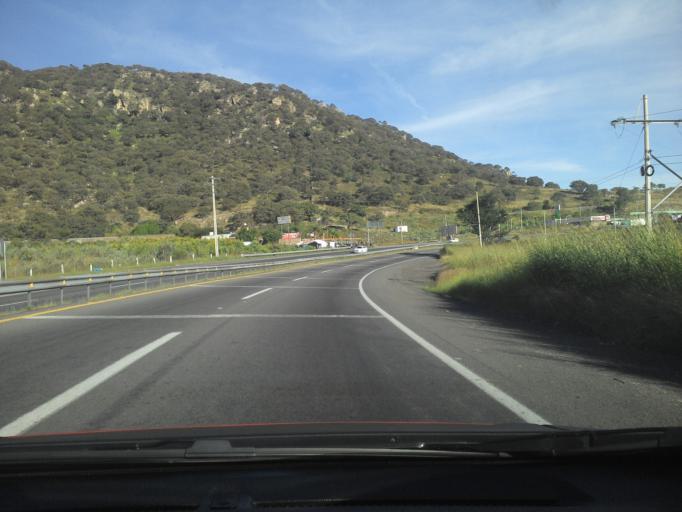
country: MX
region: Jalisco
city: La Venta del Astillero
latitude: 20.7361
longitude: -103.5804
